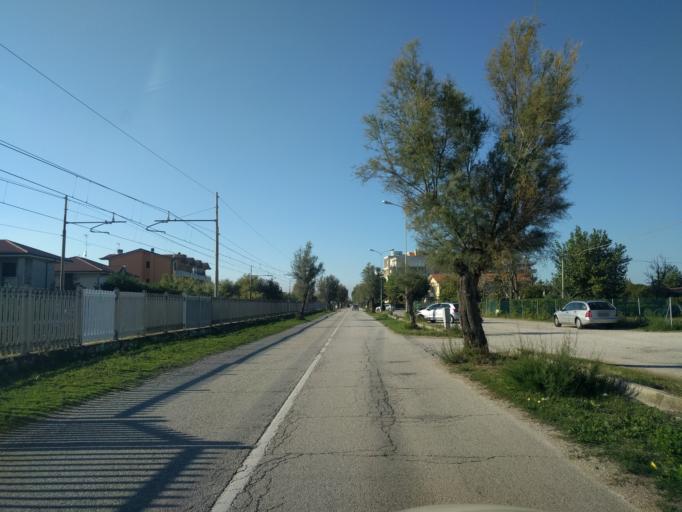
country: IT
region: The Marches
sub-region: Provincia di Pesaro e Urbino
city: Marotta
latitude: 43.7905
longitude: 13.1067
